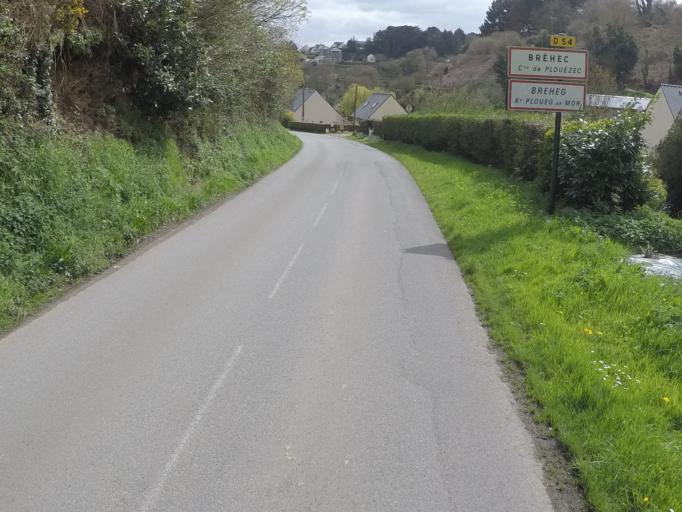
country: FR
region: Brittany
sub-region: Departement des Cotes-d'Armor
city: Plouezec
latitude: 48.7304
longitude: -2.9511
